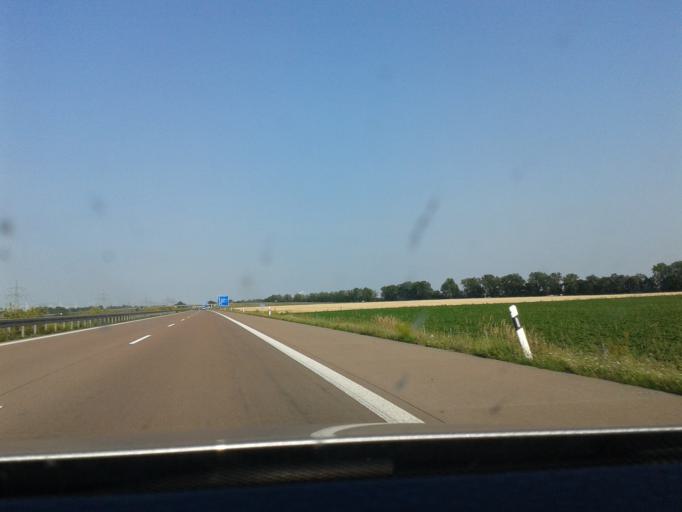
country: DE
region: Saxony-Anhalt
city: Schafstadt
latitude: 51.3999
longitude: 11.7555
